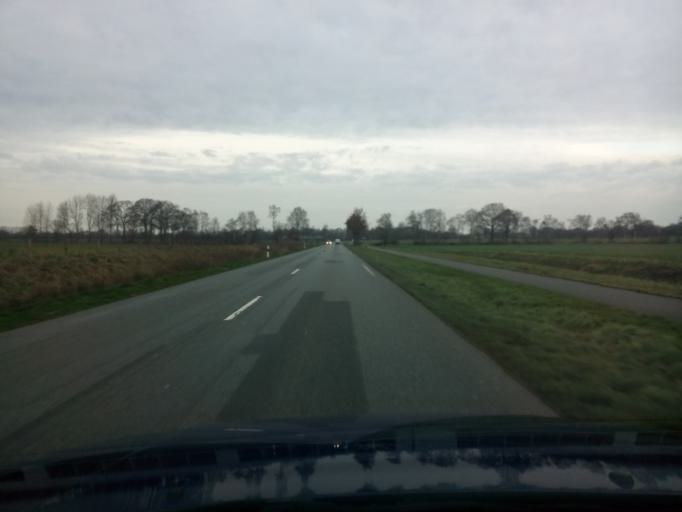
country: DE
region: Lower Saxony
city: Kuhrstedt
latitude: 53.6166
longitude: 8.8208
